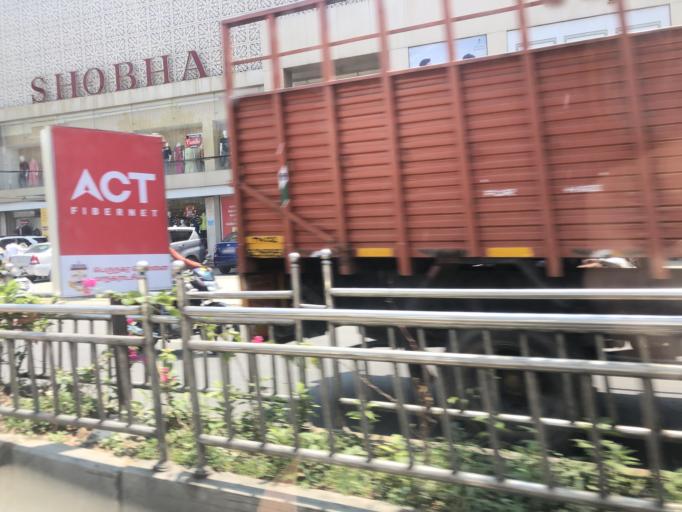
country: IN
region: Tamil Nadu
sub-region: Chennai
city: Gandhi Nagar
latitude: 12.9898
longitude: 80.2559
